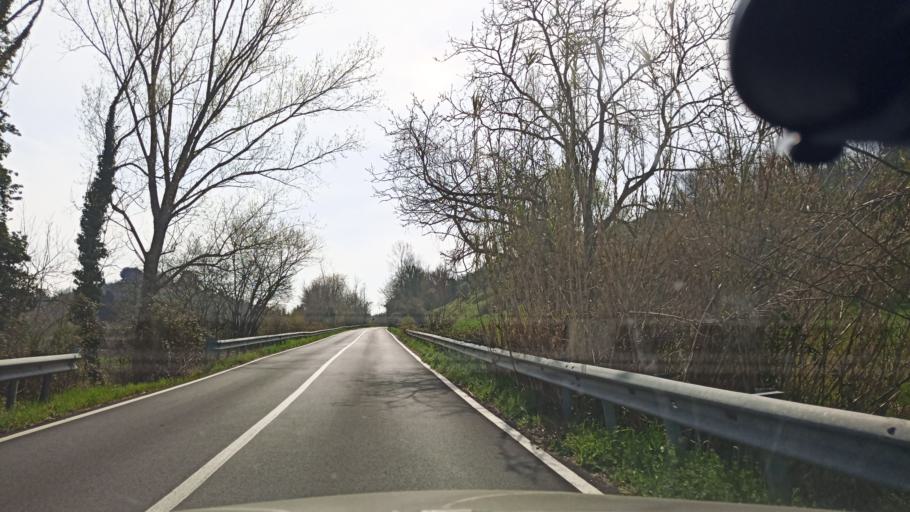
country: IT
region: Latium
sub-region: Provincia di Rieti
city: Cantalupo in Sabina
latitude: 42.3160
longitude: 12.6445
